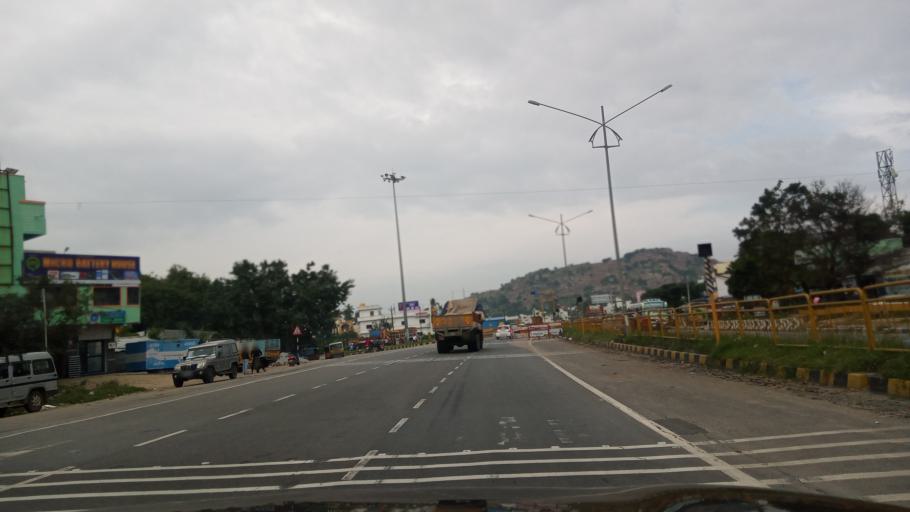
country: IN
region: Tamil Nadu
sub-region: Krishnagiri
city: Krishnagiri
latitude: 12.5227
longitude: 78.2315
